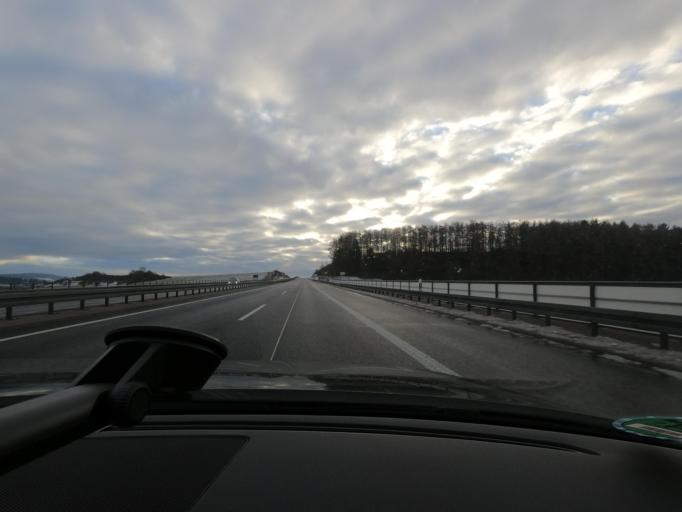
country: DE
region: Thuringia
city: Eisfeld
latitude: 50.4541
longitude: 10.8608
